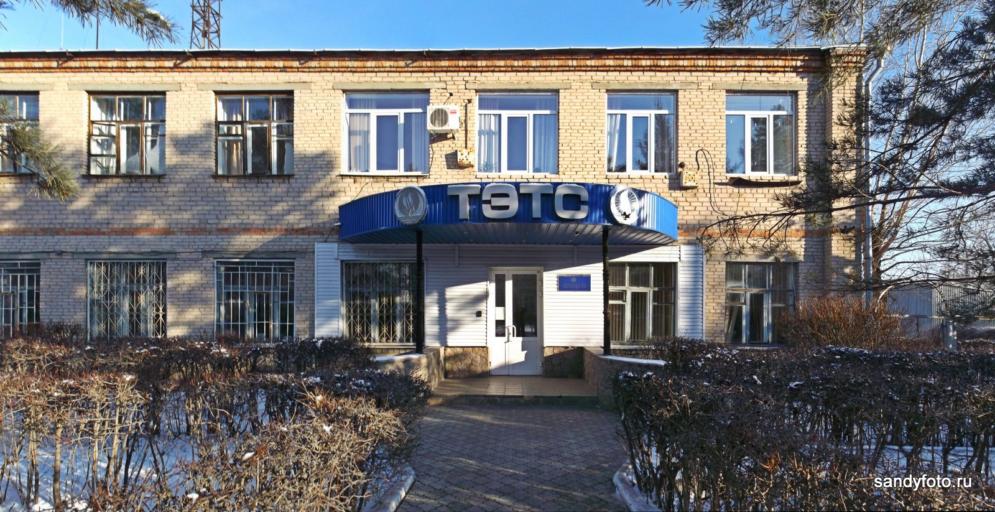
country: RU
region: Chelyabinsk
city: Troitsk
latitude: 54.0856
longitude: 61.5775
